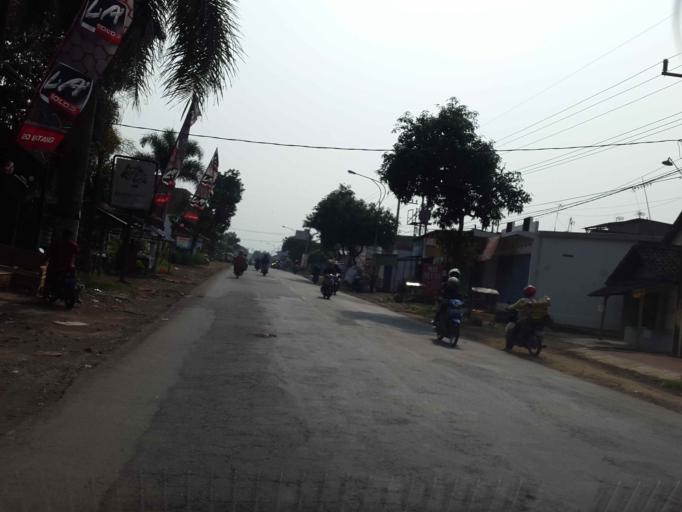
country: ID
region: East Java
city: Tamiajeng
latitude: -7.9539
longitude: 112.7010
